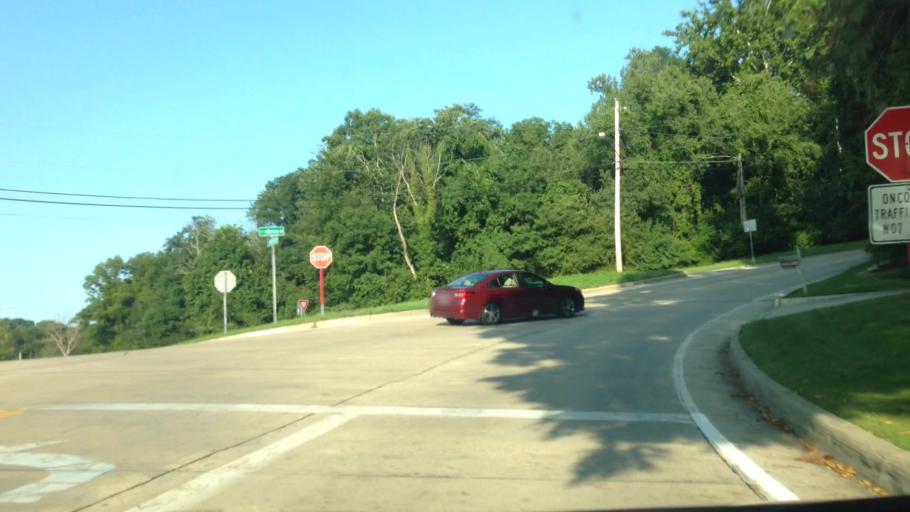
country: US
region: Ohio
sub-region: Summit County
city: Fairlawn
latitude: 41.1602
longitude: -81.5990
